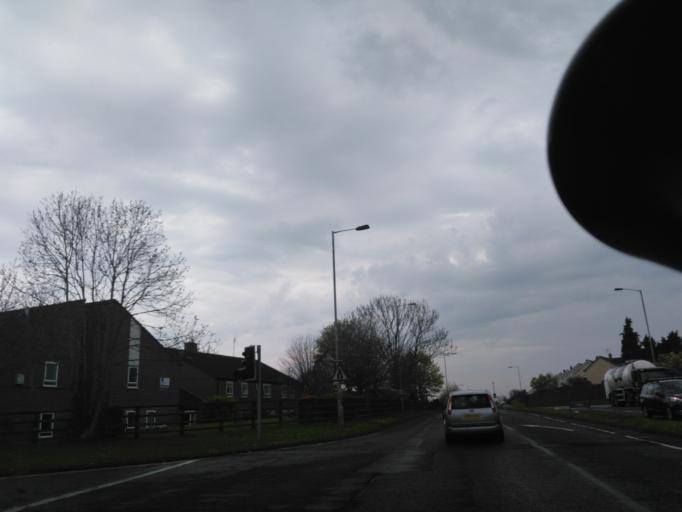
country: GB
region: England
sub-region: Somerset
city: Street
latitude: 51.1300
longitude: -2.7425
